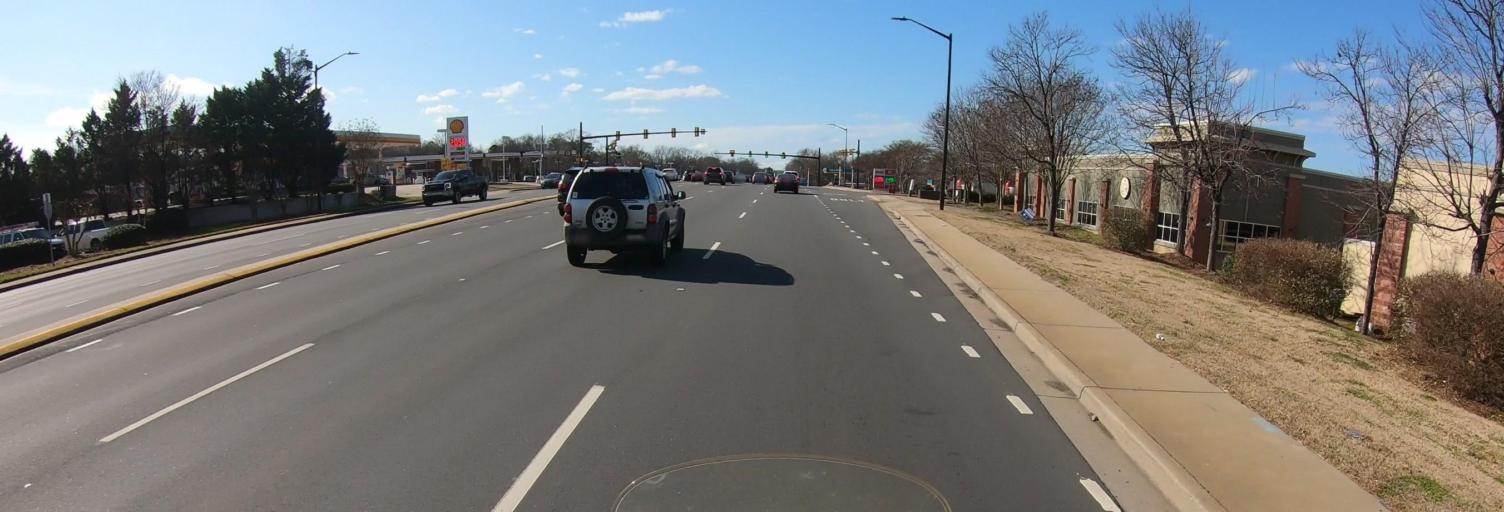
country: US
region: South Carolina
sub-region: York County
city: India Hook
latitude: 34.9767
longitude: -80.9937
